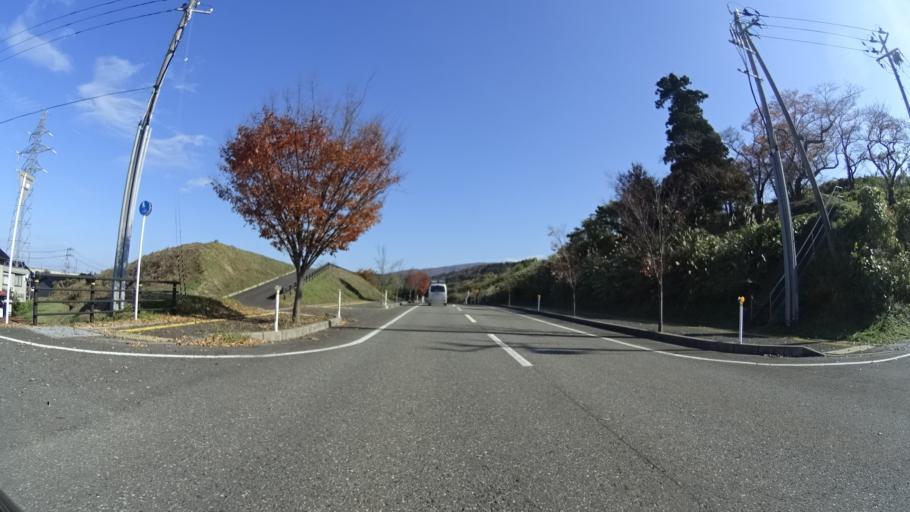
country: JP
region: Niigata
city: Itoigawa
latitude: 37.0486
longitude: 137.8916
